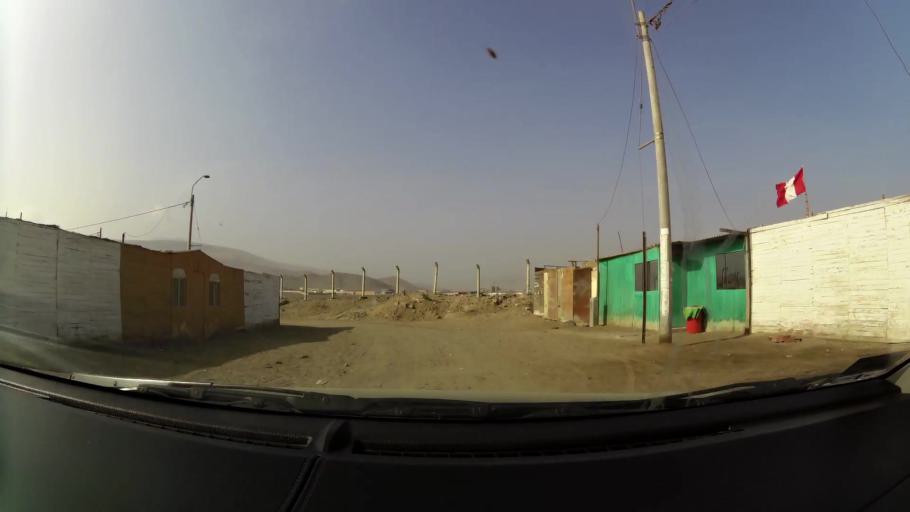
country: PE
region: Lima
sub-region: Lima
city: Santa Rosa
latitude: -11.7631
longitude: -77.1663
